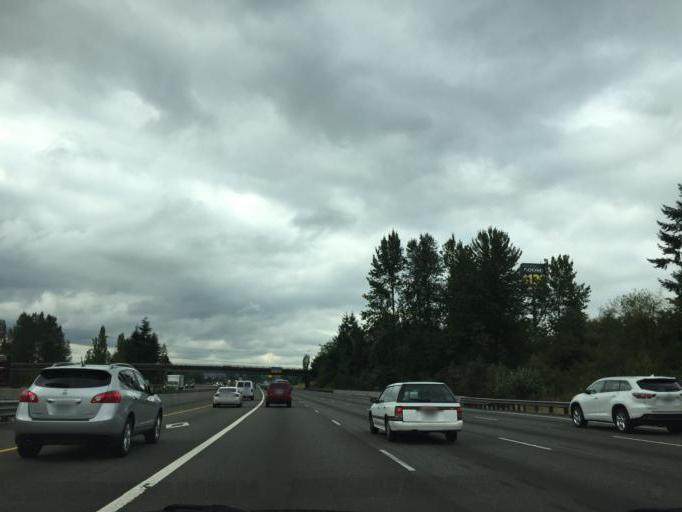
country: US
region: Washington
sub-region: Pierce County
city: Fife Heights
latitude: 47.2533
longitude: -122.3325
